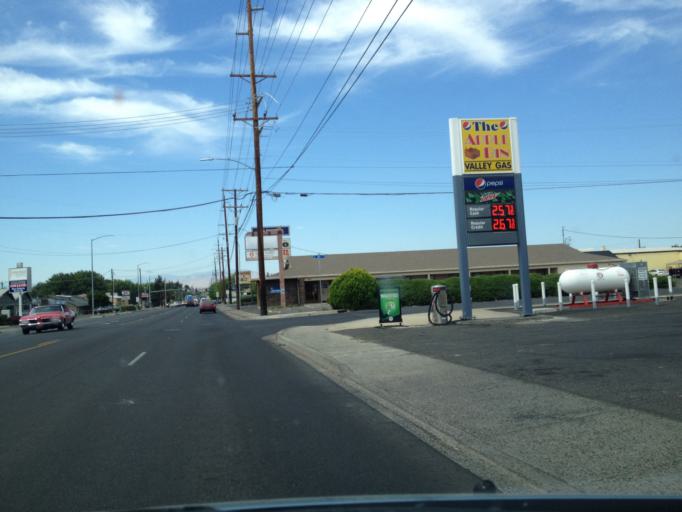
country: US
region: Washington
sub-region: Yakima County
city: West Valley
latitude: 46.5855
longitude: -120.5587
